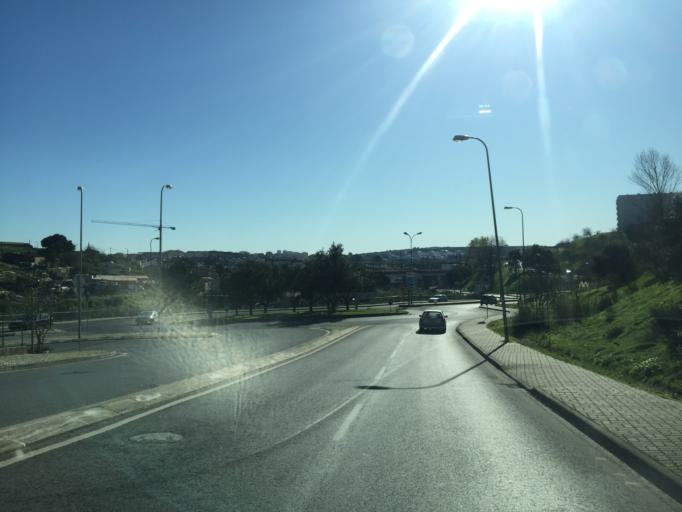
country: PT
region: Lisbon
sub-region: Sintra
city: Queluz
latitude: 38.7637
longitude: -9.2520
